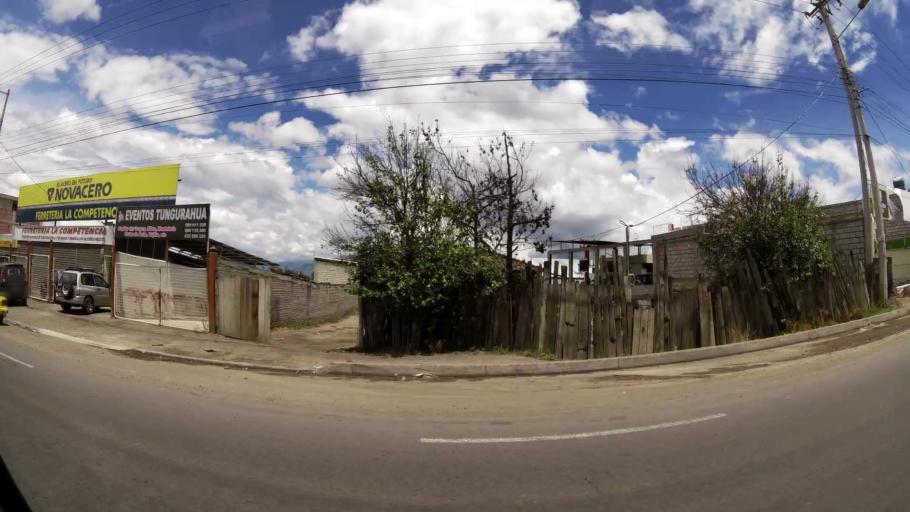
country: EC
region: Tungurahua
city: Ambato
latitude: -1.2886
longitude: -78.6062
